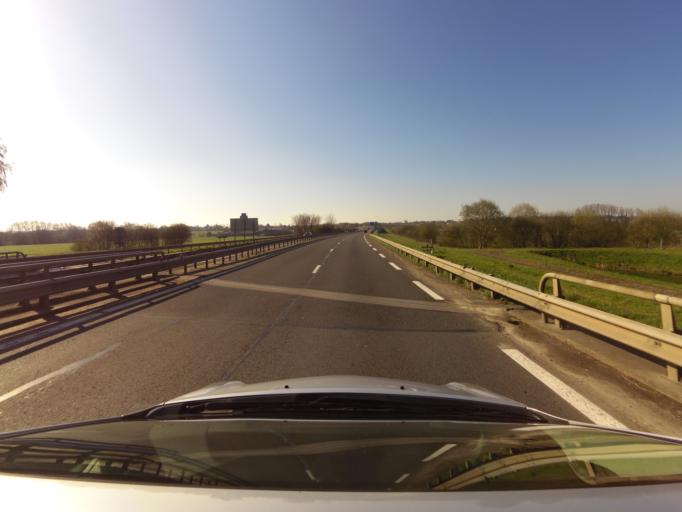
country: FR
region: Lower Normandy
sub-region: Departement de la Manche
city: Saint-Quentin-sur-le-Homme
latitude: 48.6390
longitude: -1.3415
